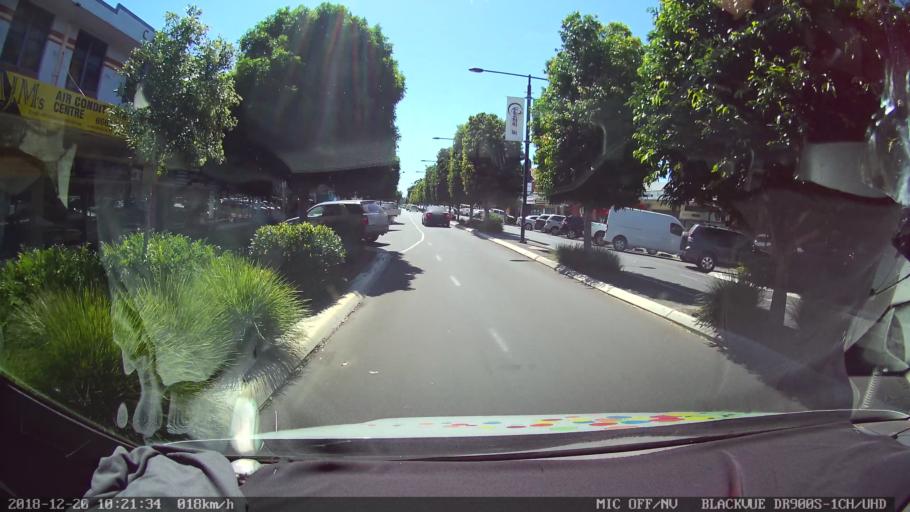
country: AU
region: New South Wales
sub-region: Richmond Valley
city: Casino
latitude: -28.8646
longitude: 153.0459
